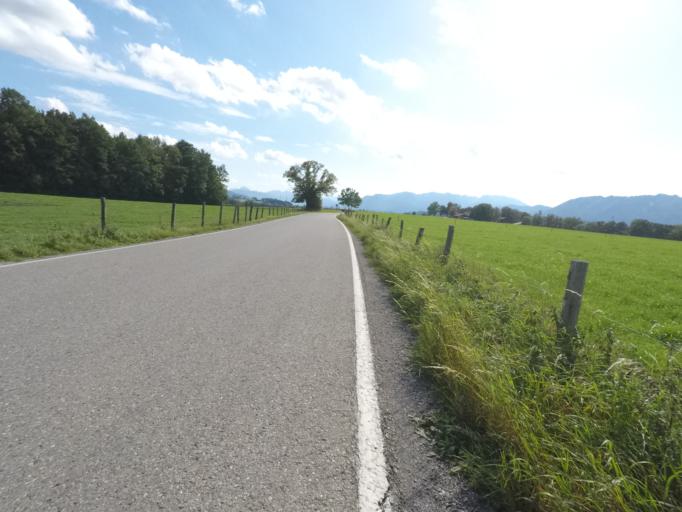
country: DE
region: Bavaria
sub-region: Upper Bavaria
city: Bad Toelz
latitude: 47.7716
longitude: 11.5733
